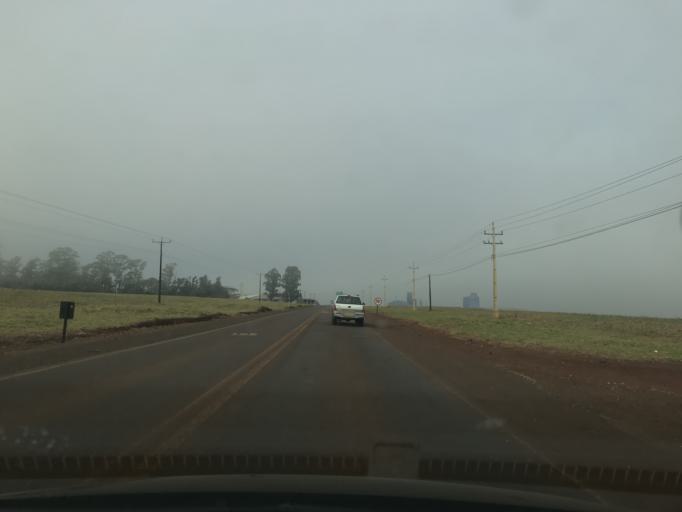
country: BR
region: Parana
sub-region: Toledo
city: Toledo
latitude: -24.7068
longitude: -53.6991
